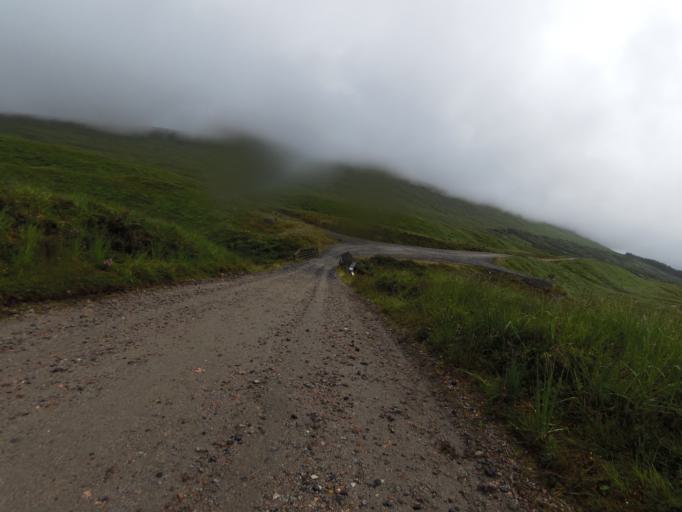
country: GB
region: Scotland
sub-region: Highland
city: Spean Bridge
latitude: 56.7676
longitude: -4.6732
